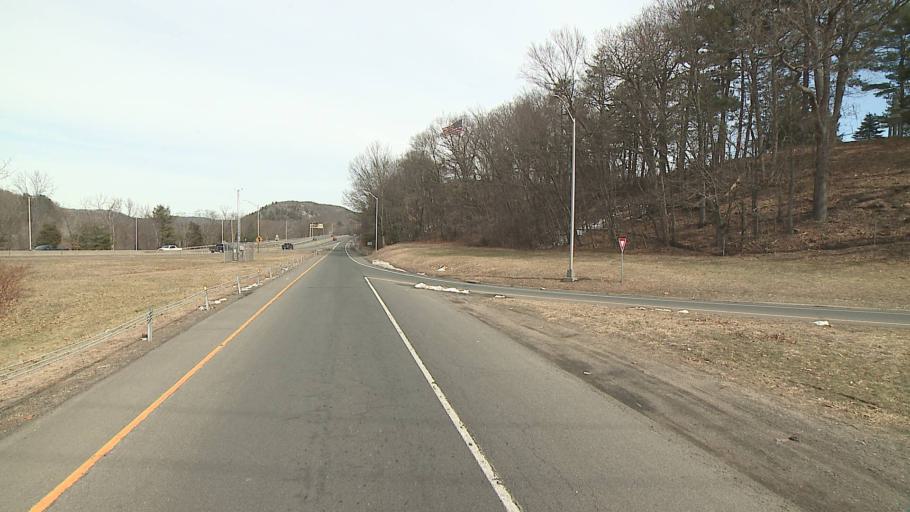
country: US
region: Connecticut
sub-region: New Haven County
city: Seymour
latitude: 41.3982
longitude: -73.0688
